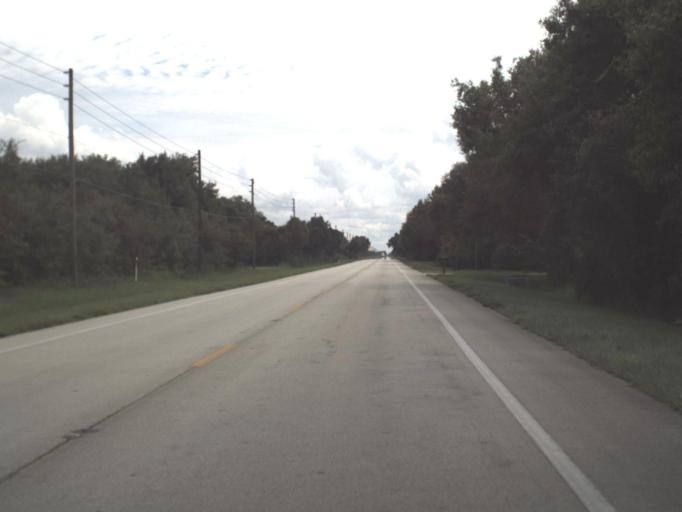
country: US
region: Florida
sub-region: DeSoto County
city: Southeast Arcadia
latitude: 27.1673
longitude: -81.8230
